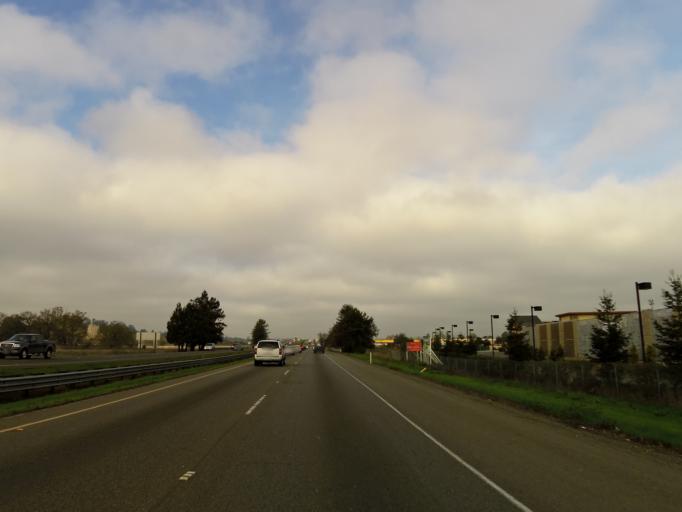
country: US
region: California
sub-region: Sonoma County
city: Petaluma
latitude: 38.2519
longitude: -122.6368
